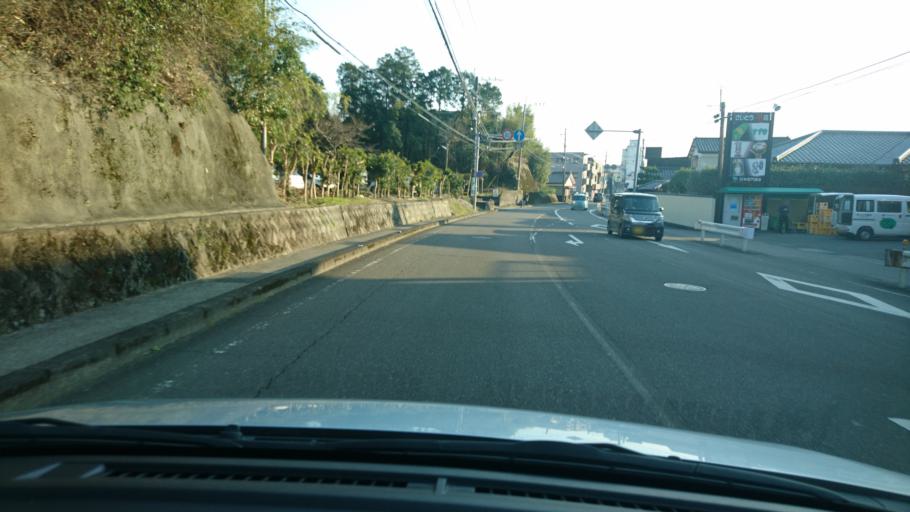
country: JP
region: Miyazaki
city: Miyazaki-shi
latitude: 31.9668
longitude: 131.4403
